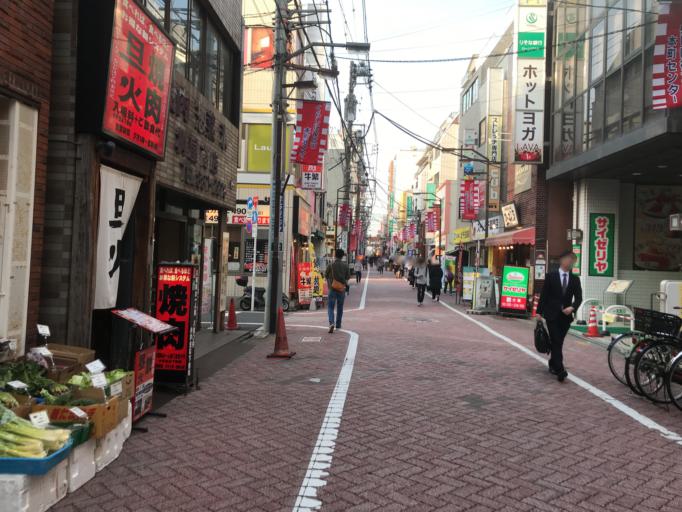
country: JP
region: Saitama
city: Soka
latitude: 35.7471
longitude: 139.8017
